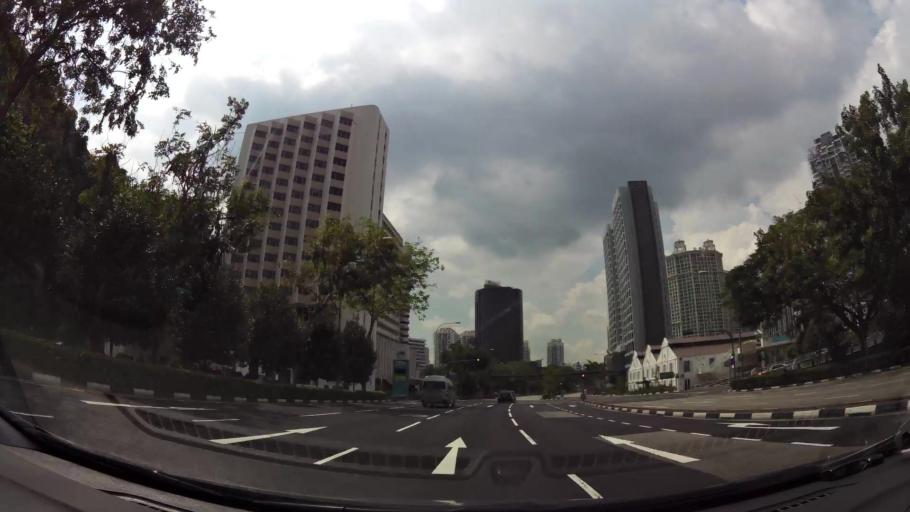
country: SG
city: Singapore
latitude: 1.2888
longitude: 103.8383
